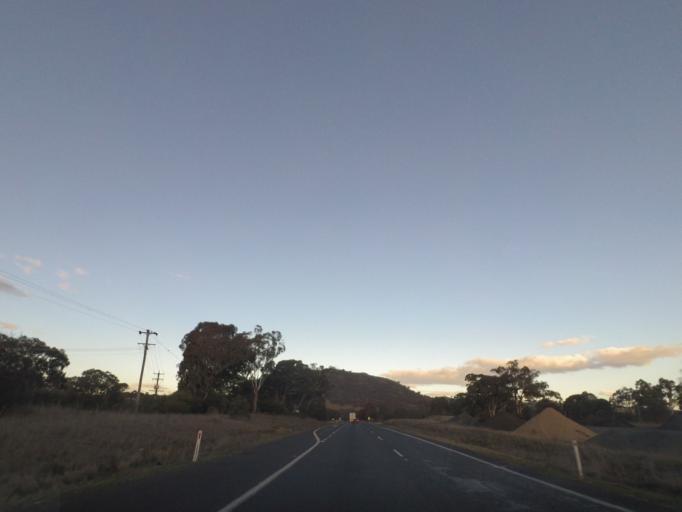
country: AU
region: New South Wales
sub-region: Yass Valley
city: Yass
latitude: -34.7713
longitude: 148.8082
